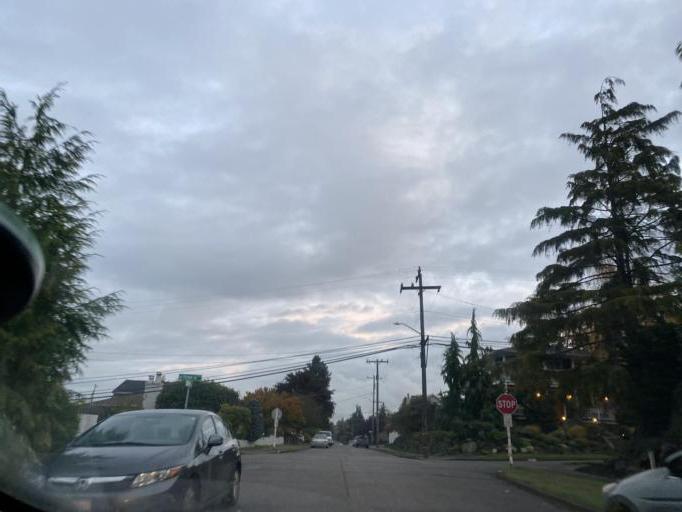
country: US
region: Washington
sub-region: King County
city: Seattle
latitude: 47.6356
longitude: -122.3957
